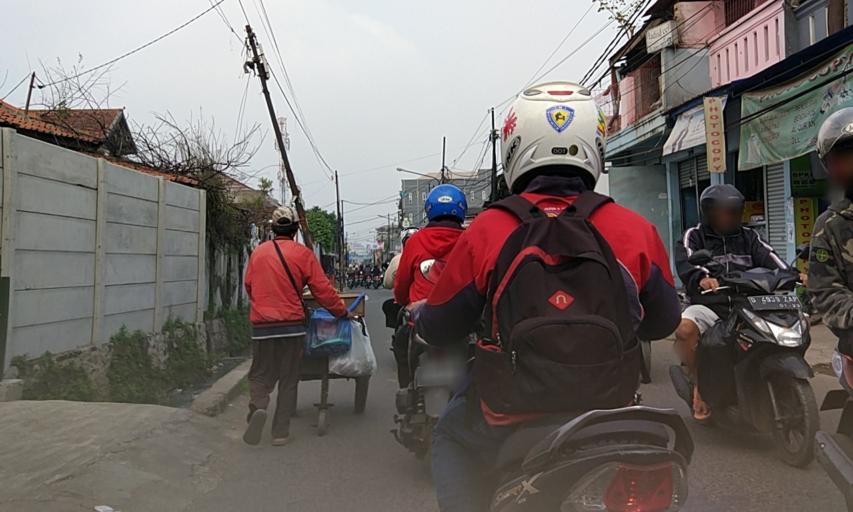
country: ID
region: West Java
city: Bandung
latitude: -6.9307
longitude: 107.5852
